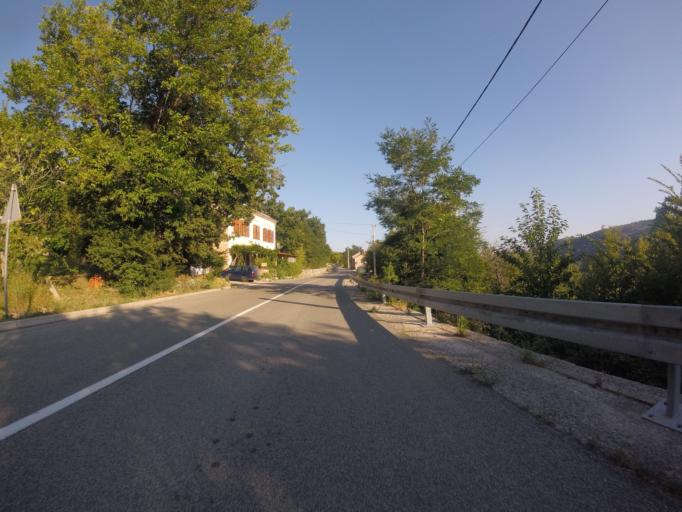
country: HR
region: Primorsko-Goranska
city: Selce
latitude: 45.1839
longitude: 14.7331
